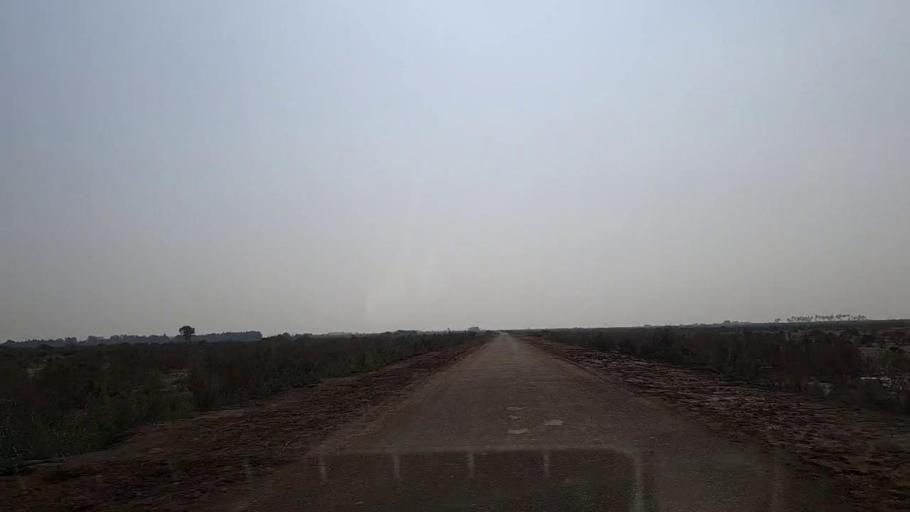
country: PK
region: Sindh
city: Mirpur Sakro
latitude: 24.6635
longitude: 67.6939
